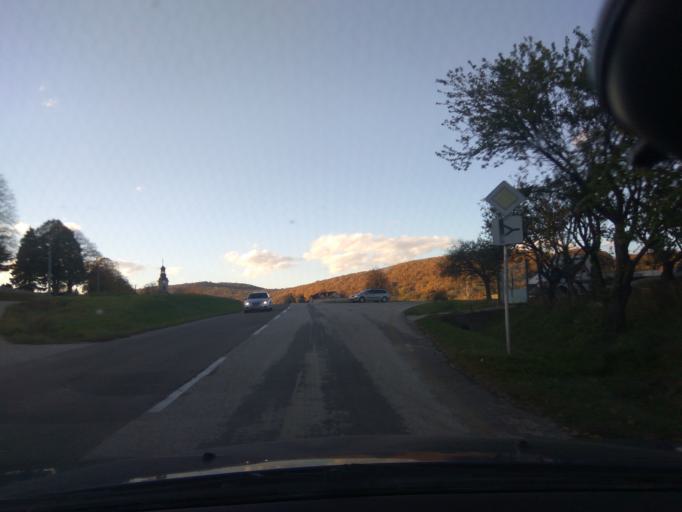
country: SK
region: Nitriansky
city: Brezova pod Bradlom
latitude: 48.6688
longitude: 17.6007
